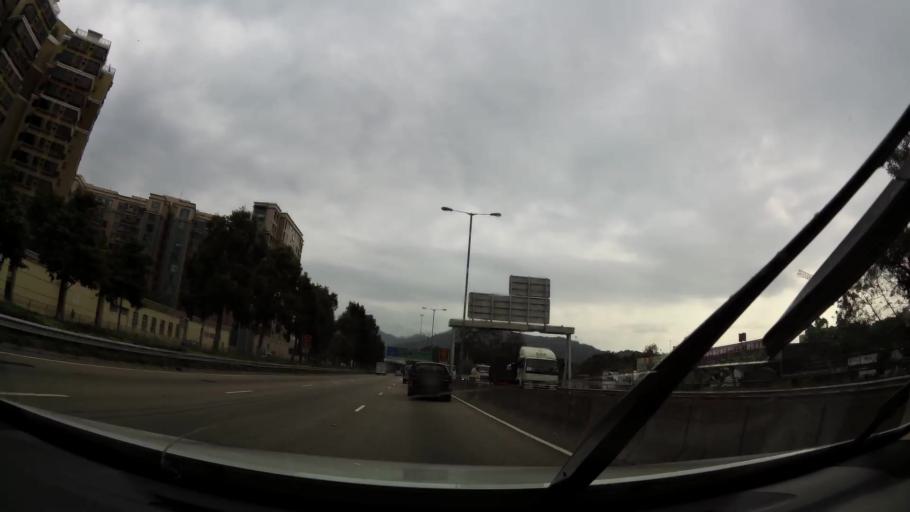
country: HK
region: Yuen Long
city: Yuen Long Kau Hui
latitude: 22.4403
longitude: 114.0161
